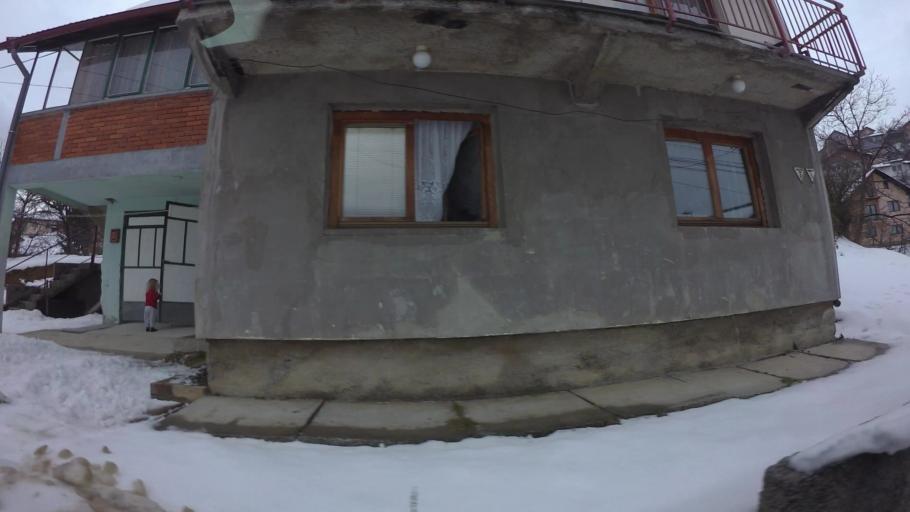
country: BA
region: Federation of Bosnia and Herzegovina
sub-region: Kanton Sarajevo
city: Sarajevo
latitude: 43.8588
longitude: 18.3595
